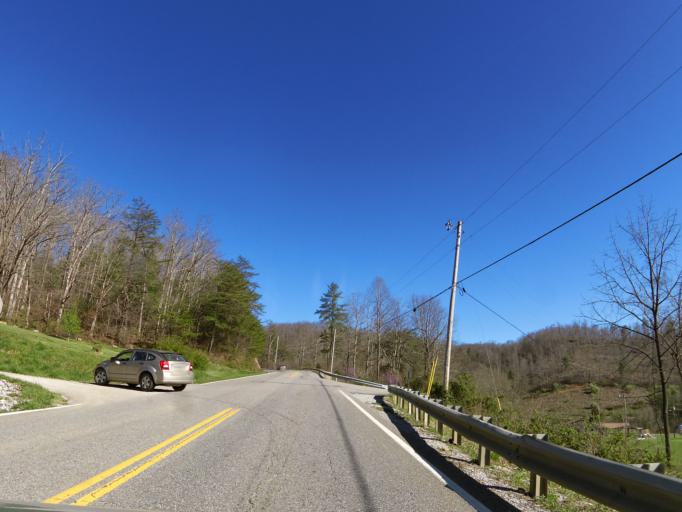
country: US
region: Tennessee
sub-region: Scott County
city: Huntsville
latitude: 36.4336
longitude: -84.4567
